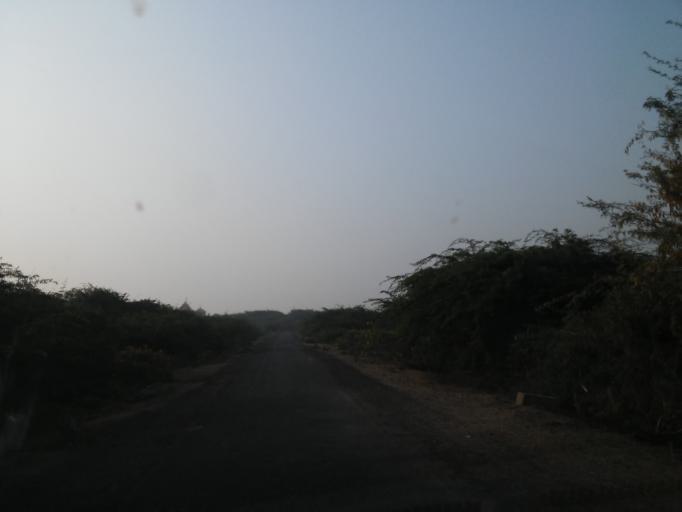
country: IN
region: Gujarat
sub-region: Kachchh
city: Mandvi
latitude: 22.8178
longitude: 69.3898
